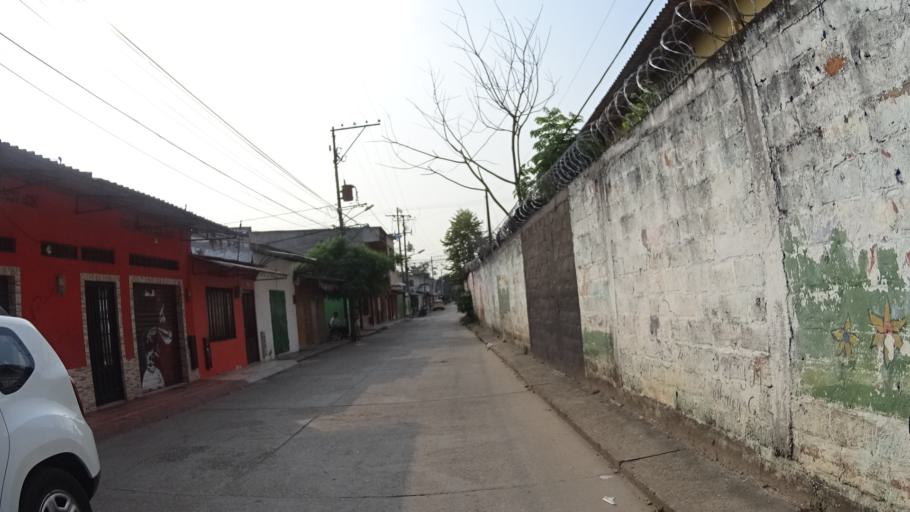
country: CO
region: Cundinamarca
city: Puerto Salgar
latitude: 5.4757
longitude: -74.6781
